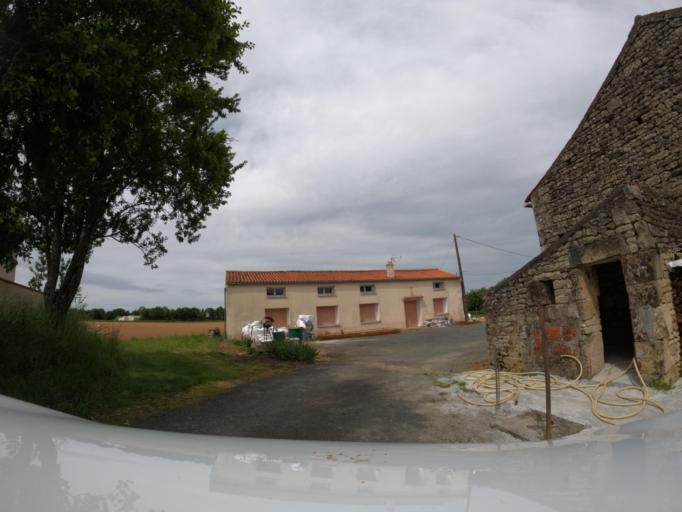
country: FR
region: Pays de la Loire
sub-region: Departement de la Vendee
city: Saint-Hilaire-des-Loges
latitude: 46.4911
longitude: -0.6341
